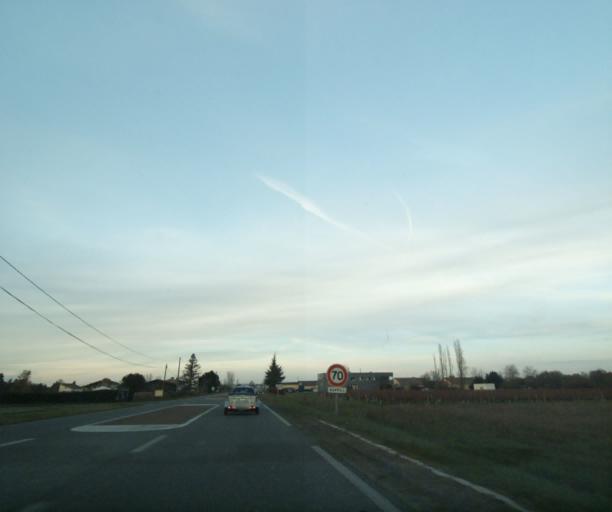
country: FR
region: Aquitaine
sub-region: Departement de la Gironde
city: Langon
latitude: 44.5265
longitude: -0.2405
